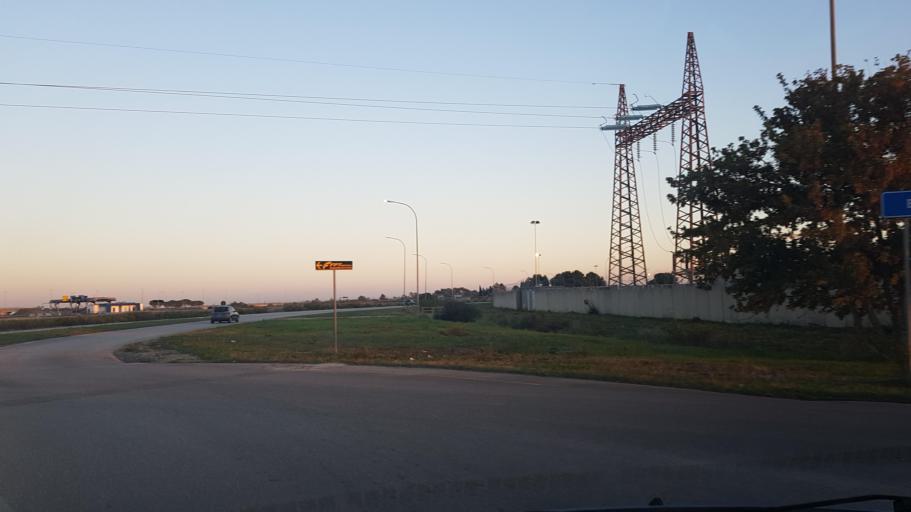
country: IT
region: Apulia
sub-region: Provincia di Foggia
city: Carapelle
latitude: 41.4255
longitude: 15.6508
